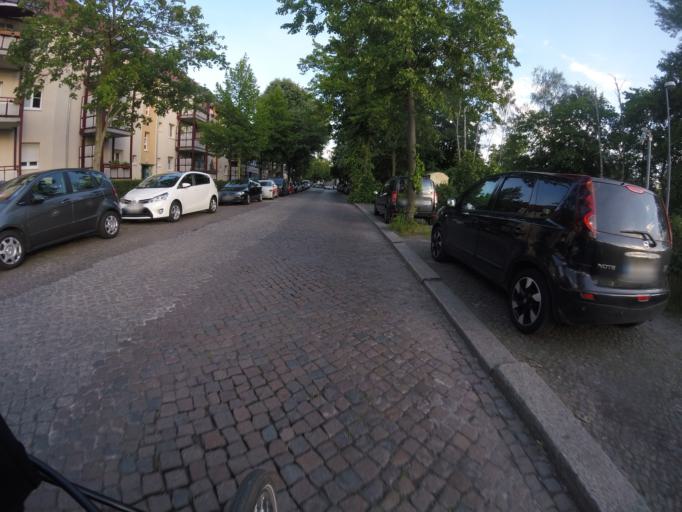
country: DE
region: Berlin
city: Tegel
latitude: 52.5806
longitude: 13.2872
